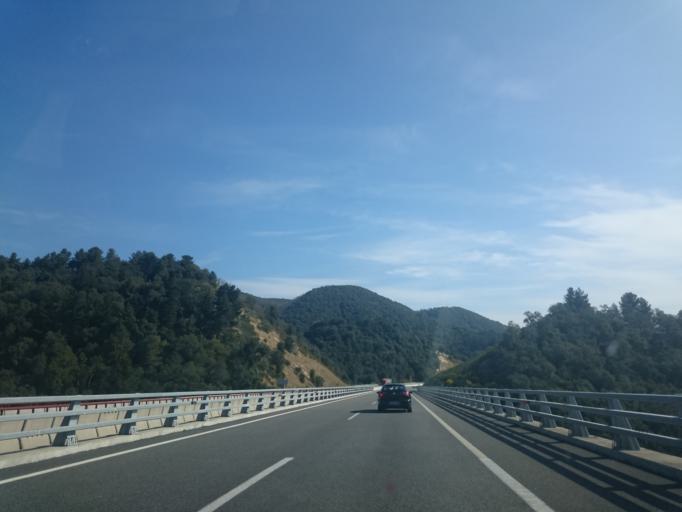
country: ES
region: Catalonia
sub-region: Provincia de Girona
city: Arbucies
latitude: 41.8497
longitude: 2.4760
